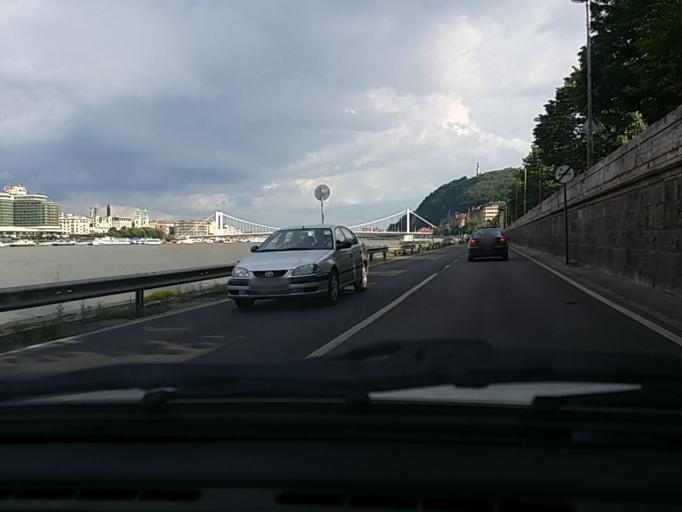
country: HU
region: Budapest
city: Budapest
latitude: 47.4977
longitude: 19.0417
